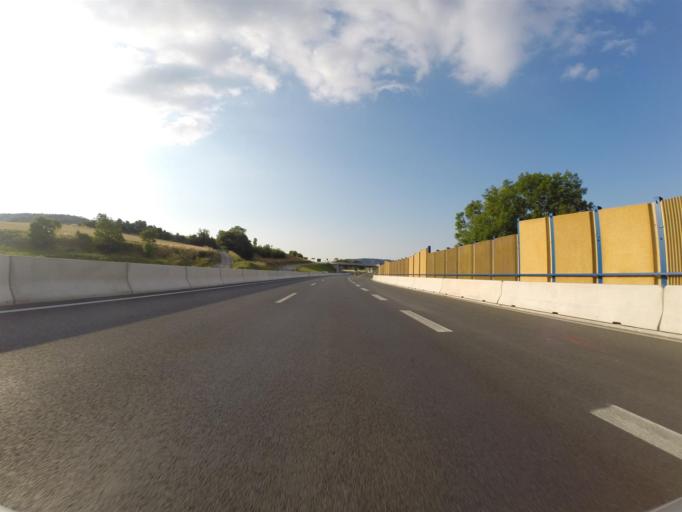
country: DE
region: Thuringia
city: Rothenstein
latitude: 50.8681
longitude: 11.5977
